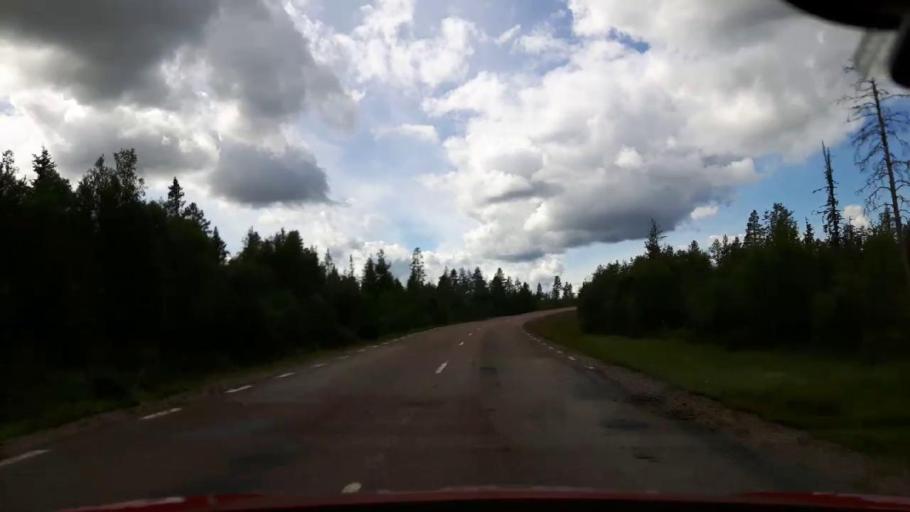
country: SE
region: Jaemtland
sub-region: Harjedalens Kommun
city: Sveg
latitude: 61.8231
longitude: 13.8611
